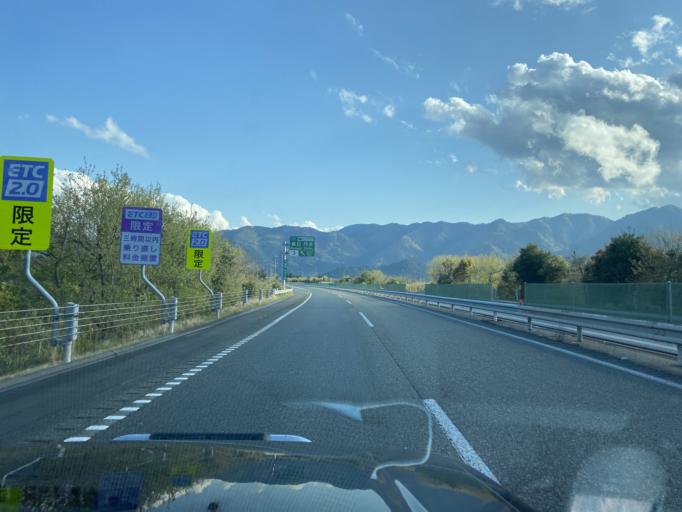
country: JP
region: Kyoto
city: Fukuchiyama
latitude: 35.1692
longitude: 135.1195
